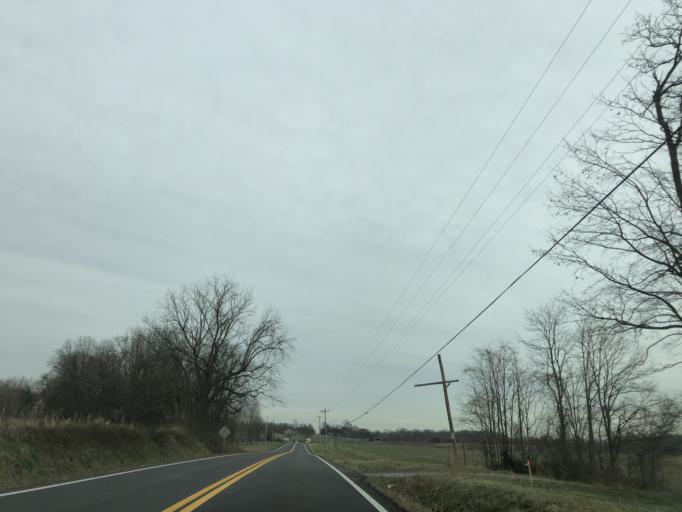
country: US
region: Tennessee
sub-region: Sumner County
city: White House
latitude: 36.4766
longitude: -86.7236
